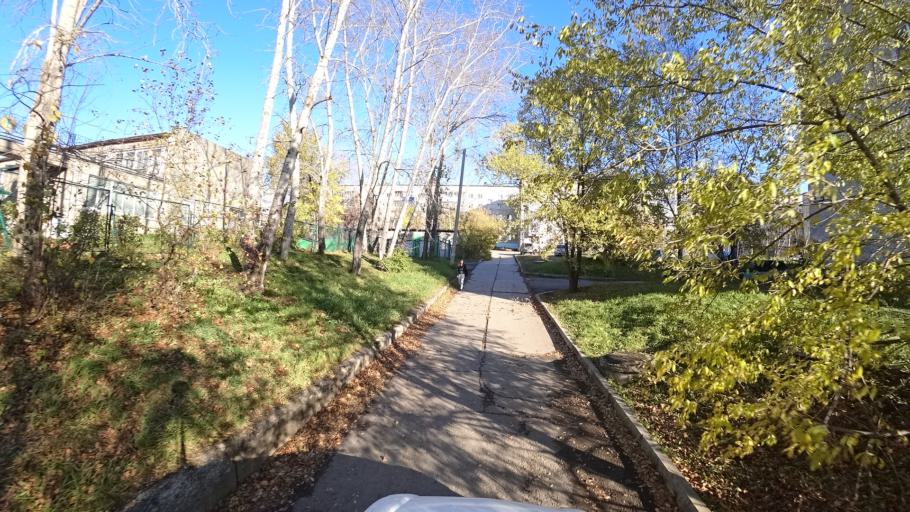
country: RU
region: Khabarovsk Krai
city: Amursk
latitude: 50.2297
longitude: 136.9099
